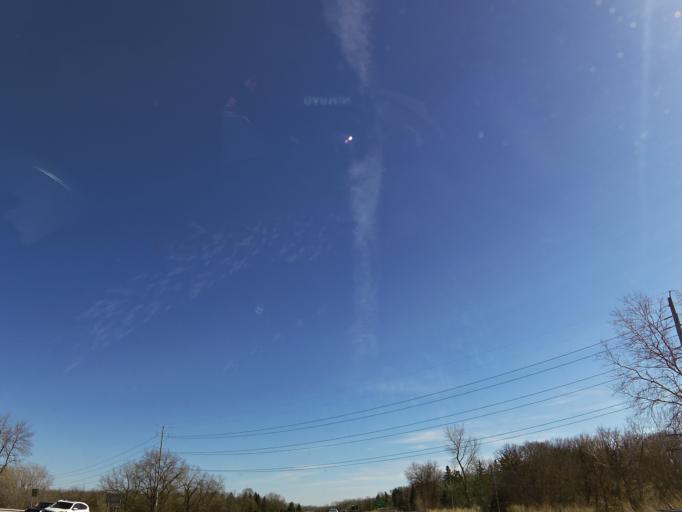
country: US
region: Minnesota
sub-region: Hennepin County
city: Plymouth
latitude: 44.9967
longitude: -93.4394
